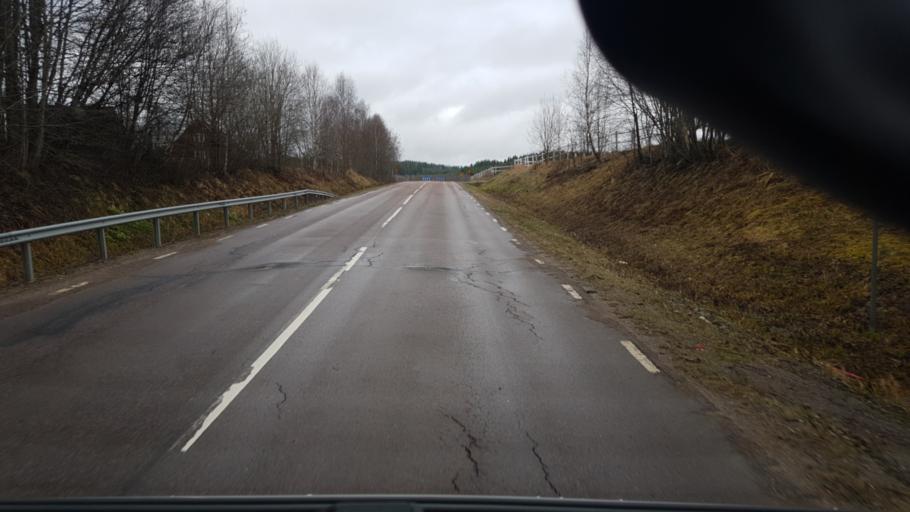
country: SE
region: Vaermland
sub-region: Eda Kommun
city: Charlottenberg
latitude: 59.9203
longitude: 12.2858
